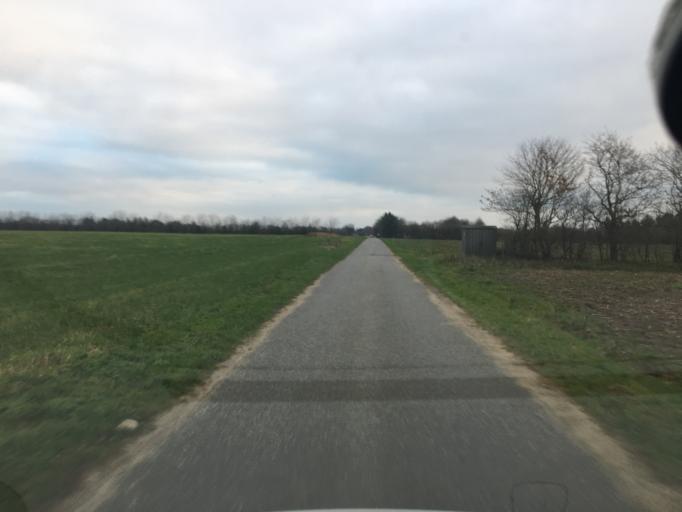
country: DK
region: South Denmark
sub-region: Tonder Kommune
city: Logumkloster
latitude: 55.0311
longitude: 9.0323
